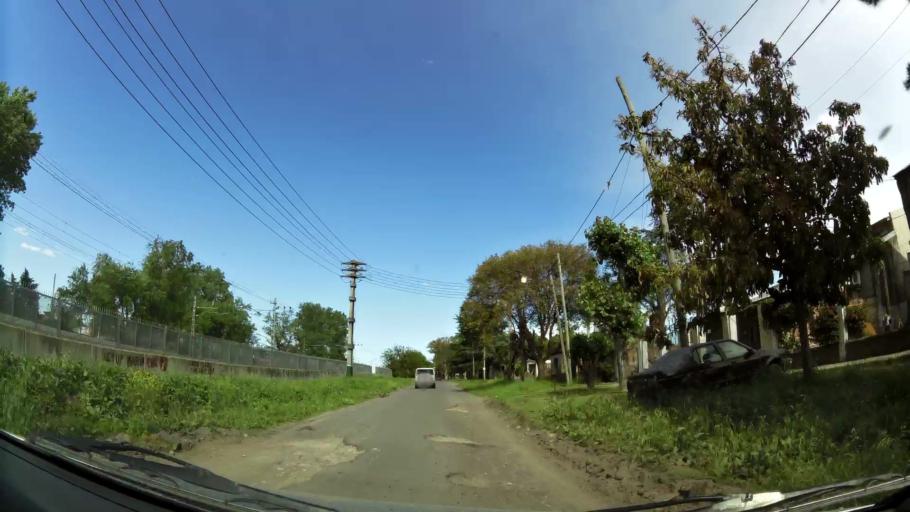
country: AR
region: Buenos Aires
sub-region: Partido de Almirante Brown
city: Adrogue
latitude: -34.8003
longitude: -58.3440
